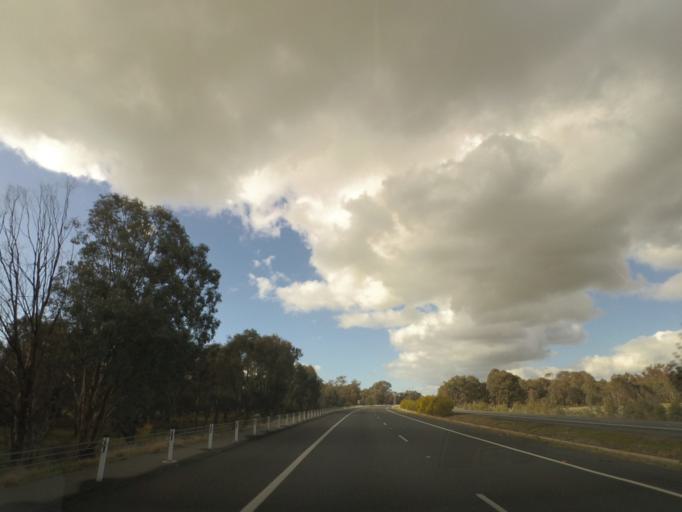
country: AU
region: New South Wales
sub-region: Greater Hume Shire
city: Holbrook
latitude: -35.7069
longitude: 147.3103
